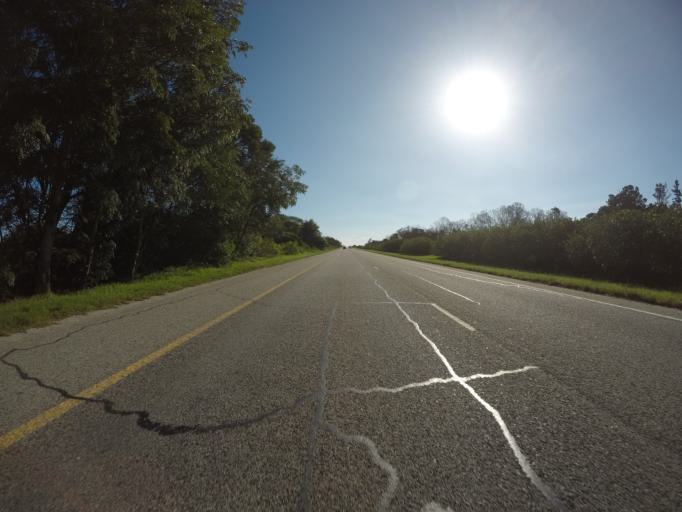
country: ZA
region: Eastern Cape
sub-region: Nelson Mandela Bay Metropolitan Municipality
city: Port Elizabeth
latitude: -33.9426
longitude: 25.3883
